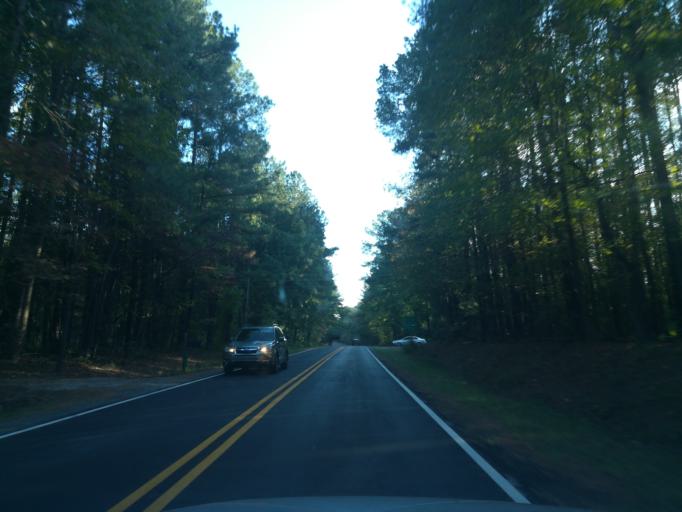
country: US
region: North Carolina
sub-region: Orange County
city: Chapel Hill
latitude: 35.9666
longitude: -79.0347
